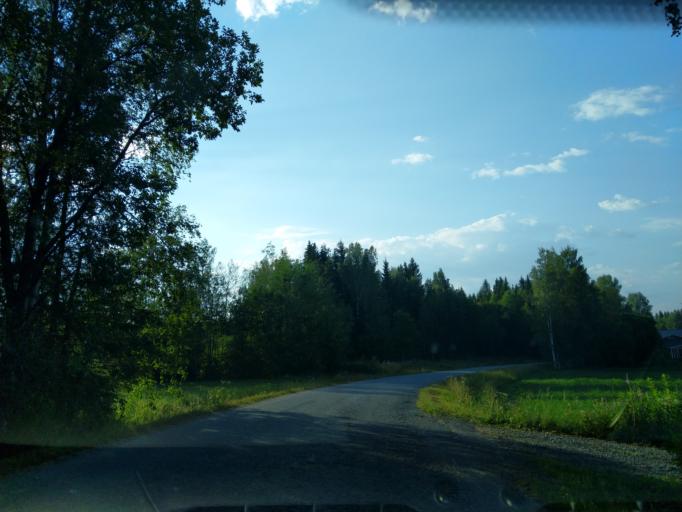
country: FI
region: Satakunta
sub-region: Pori
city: Laengelmaeki
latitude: 61.8046
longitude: 22.1913
